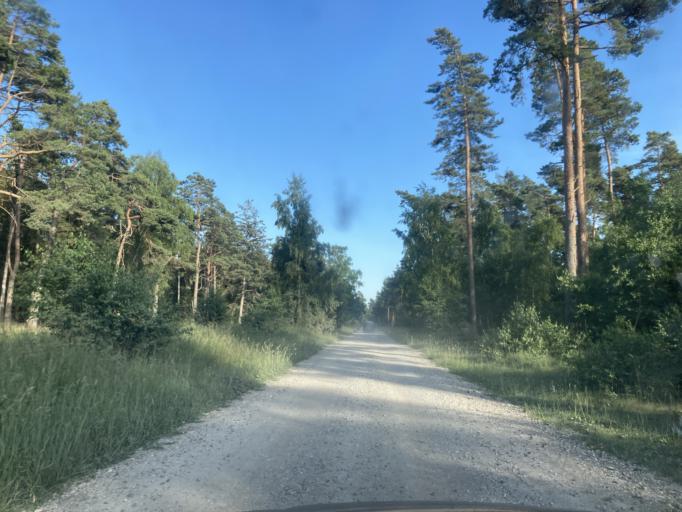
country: DK
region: Capital Region
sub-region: Halsnaes Kommune
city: Frederiksvaerk
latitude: 56.0168
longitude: 12.0119
